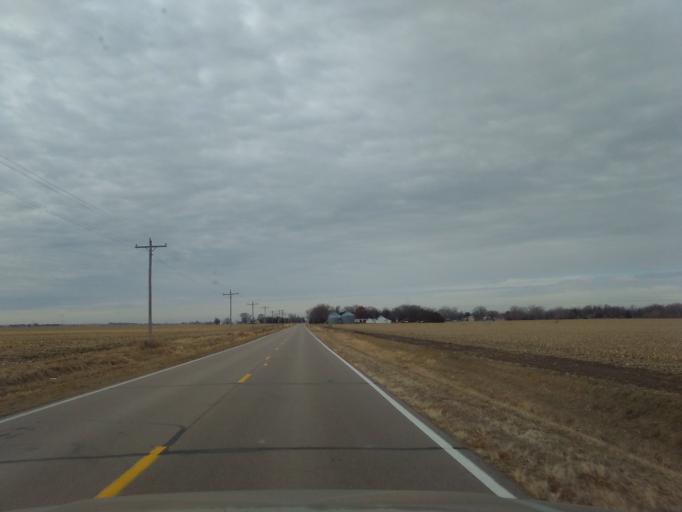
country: US
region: Nebraska
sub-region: Hall County
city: Grand Island
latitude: 40.7709
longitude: -98.4027
